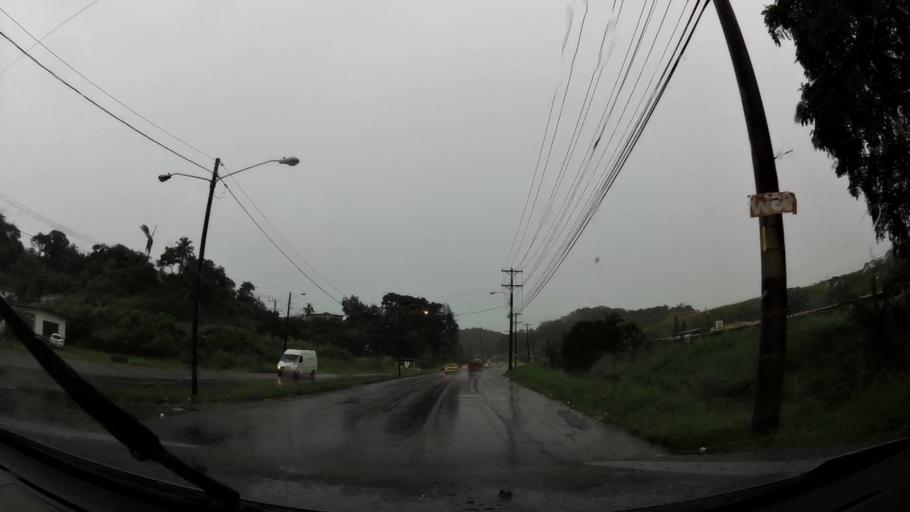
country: PA
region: Colon
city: Sabanitas
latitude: 9.3537
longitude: -79.8156
